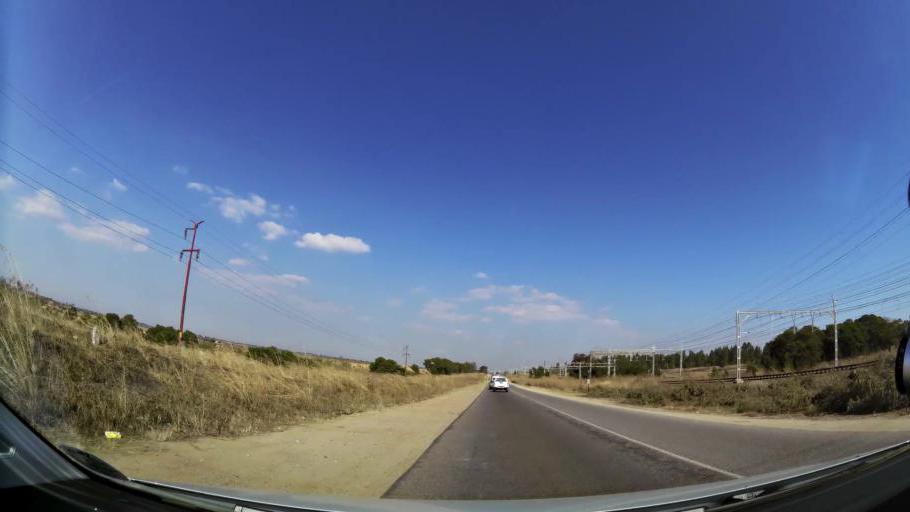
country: ZA
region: Gauteng
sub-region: Ekurhuleni Metropolitan Municipality
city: Tembisa
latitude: -26.0482
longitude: 28.2521
